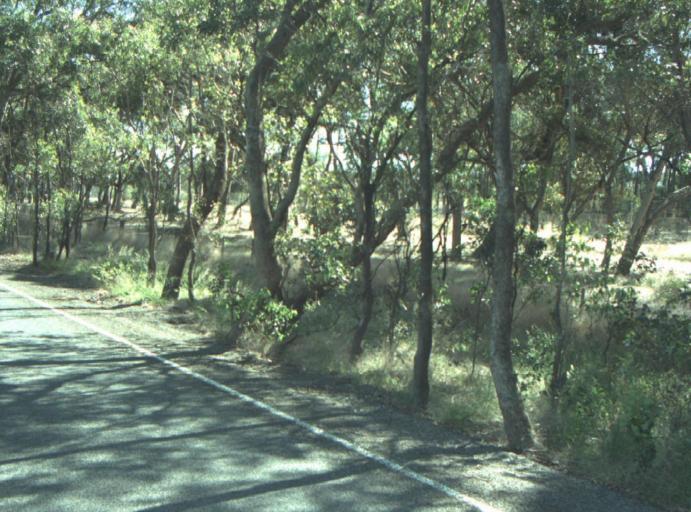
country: AU
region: Victoria
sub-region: Greater Geelong
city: Lara
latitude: -37.9173
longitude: 144.3971
